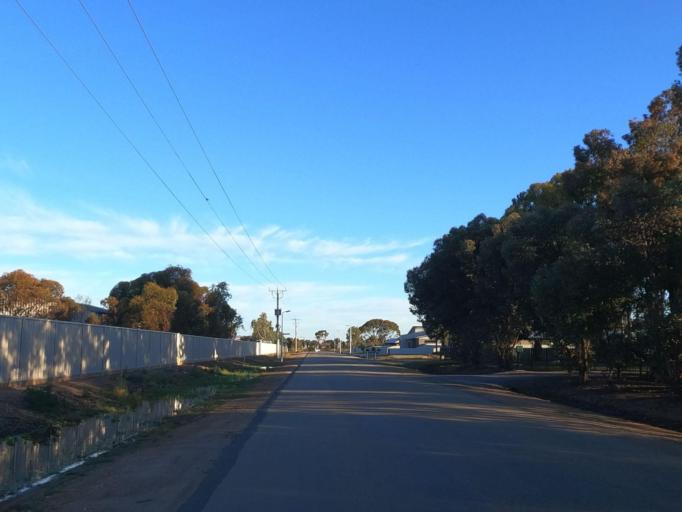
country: AU
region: Victoria
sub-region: Swan Hill
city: Swan Hill
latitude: -35.3309
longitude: 143.5345
